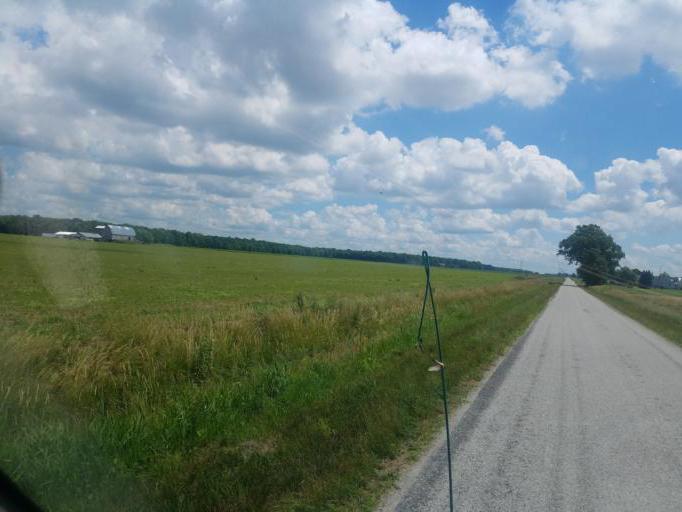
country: US
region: Ohio
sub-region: Huron County
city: Willard
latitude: 40.9939
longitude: -82.8351
